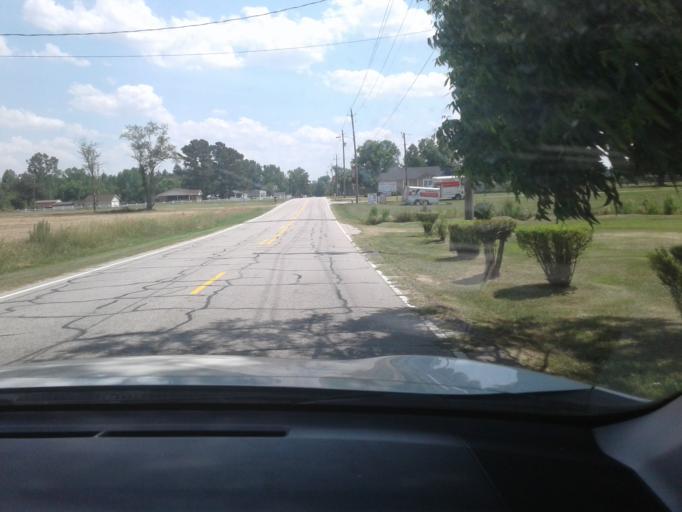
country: US
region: North Carolina
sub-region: Harnett County
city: Erwin
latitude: 35.2124
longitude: -78.6756
